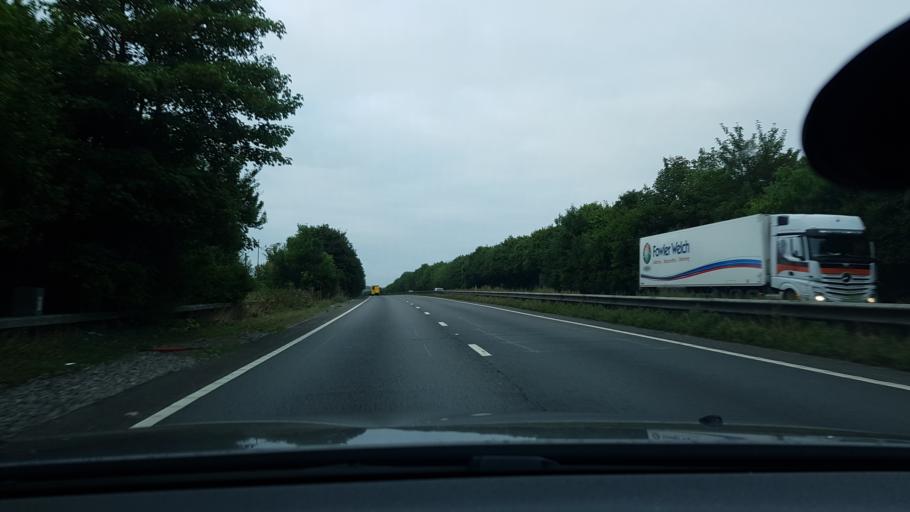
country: GB
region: England
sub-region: Hampshire
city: Kings Worthy
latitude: 51.1469
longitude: -1.3475
